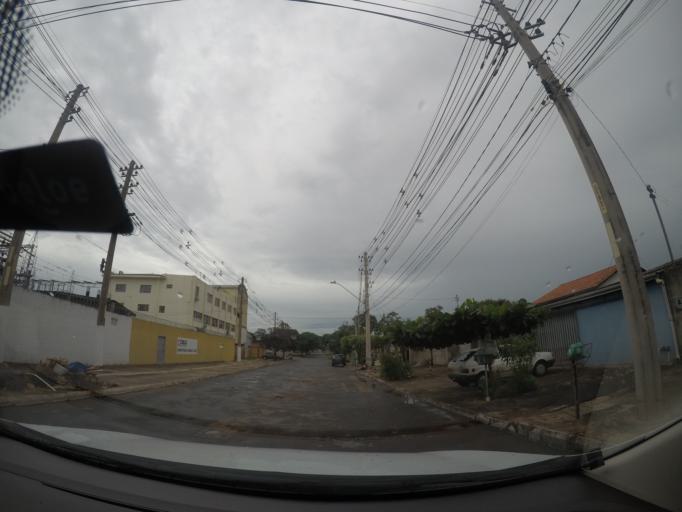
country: BR
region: Goias
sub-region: Goiania
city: Goiania
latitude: -16.6840
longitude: -49.2365
